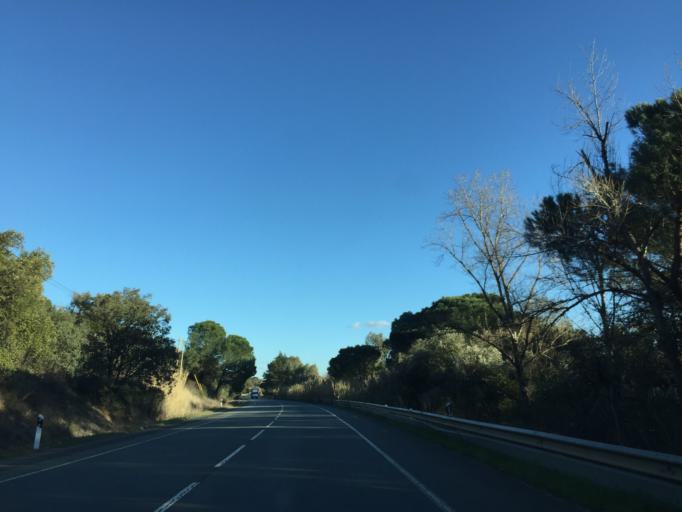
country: PT
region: Setubal
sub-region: Grandola
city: Grandola
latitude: 38.1266
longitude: -8.4622
